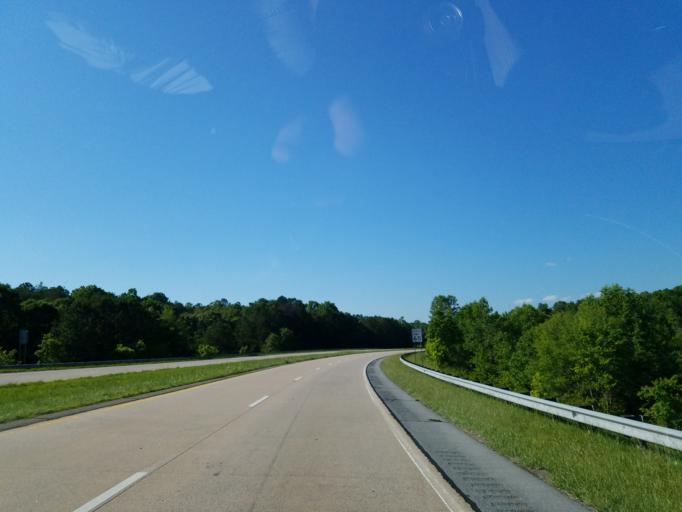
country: US
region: Georgia
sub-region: Gilmer County
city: Ellijay
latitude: 34.5895
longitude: -84.5186
